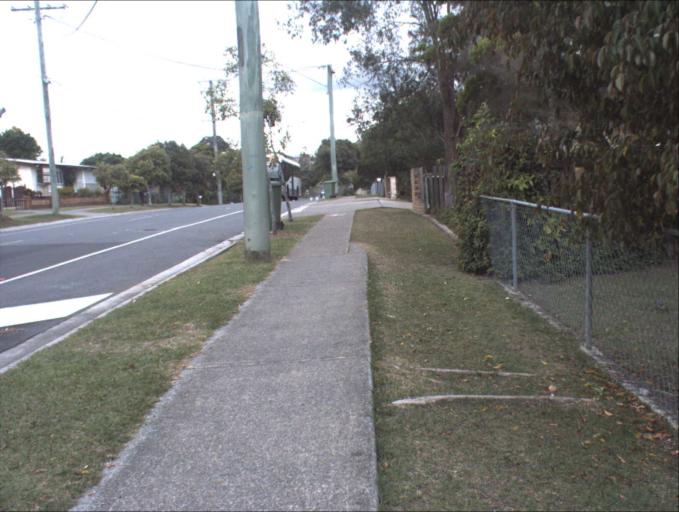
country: AU
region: Queensland
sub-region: Logan
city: Woodridge
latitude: -27.6329
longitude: 153.1029
